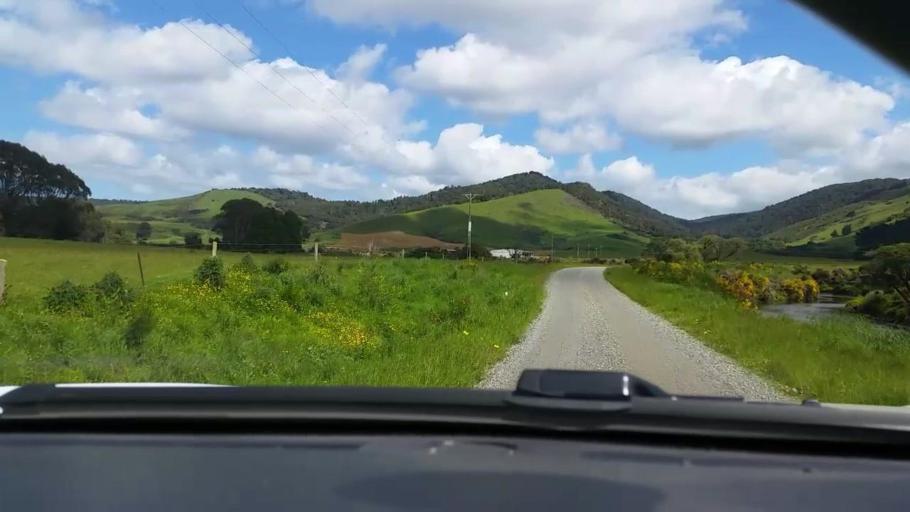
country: NZ
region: Otago
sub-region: Clutha District
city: Papatowai
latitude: -46.5901
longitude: 169.1439
